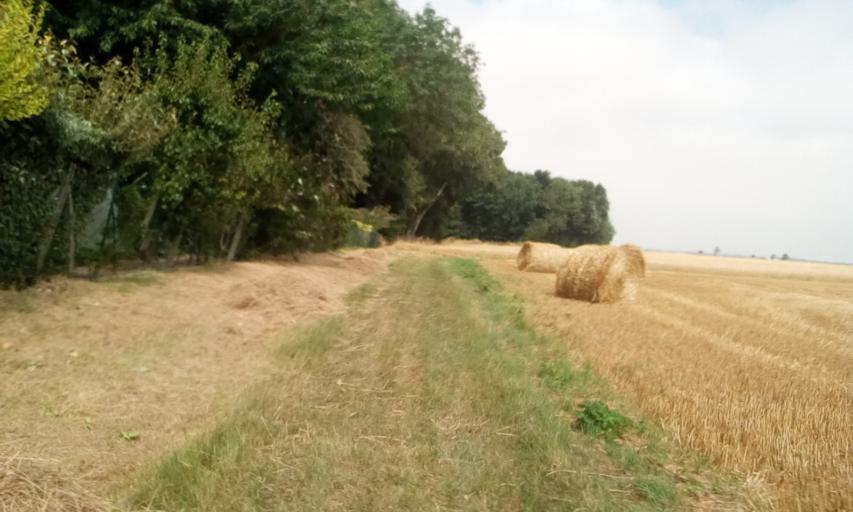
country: FR
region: Lower Normandy
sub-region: Departement du Calvados
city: Douvres-la-Delivrande
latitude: 49.2968
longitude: -0.4093
